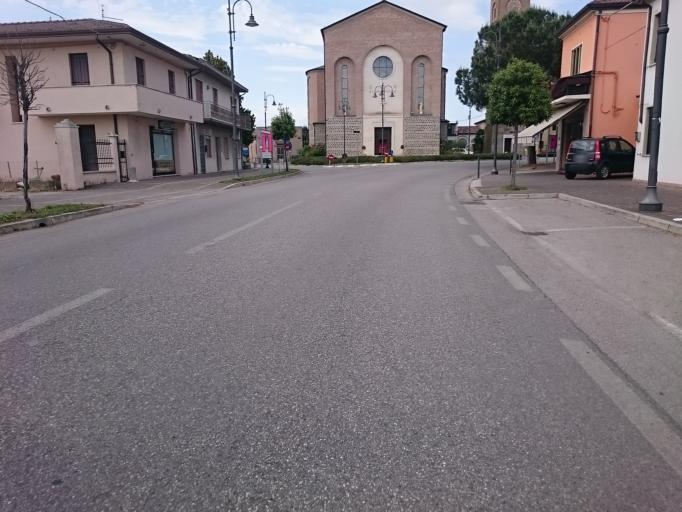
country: IT
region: Veneto
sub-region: Provincia di Padova
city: Ponso
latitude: 45.1922
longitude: 11.5864
